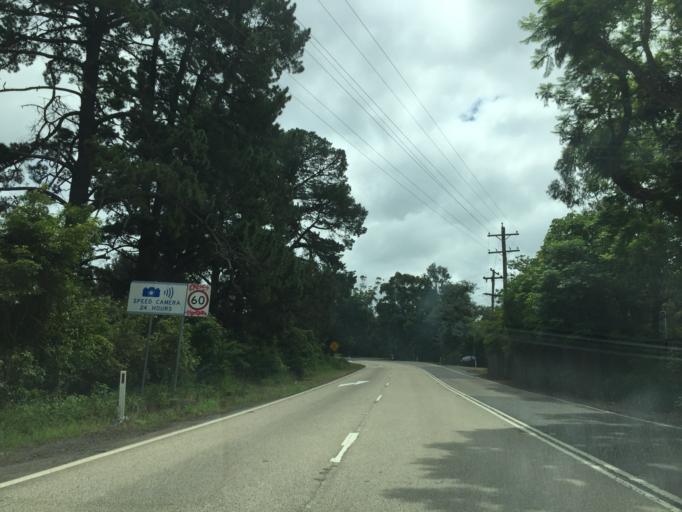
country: AU
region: New South Wales
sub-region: Hawkesbury
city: Richmond
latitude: -33.5370
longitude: 150.6330
